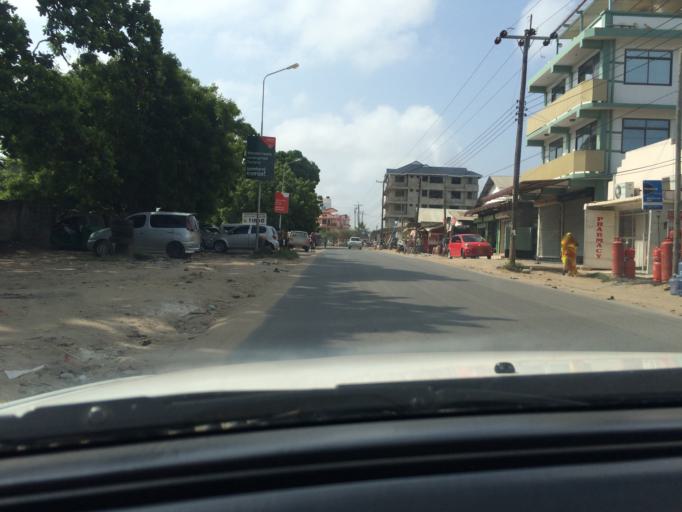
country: TZ
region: Dar es Salaam
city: Magomeni
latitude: -6.7648
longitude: 39.2691
